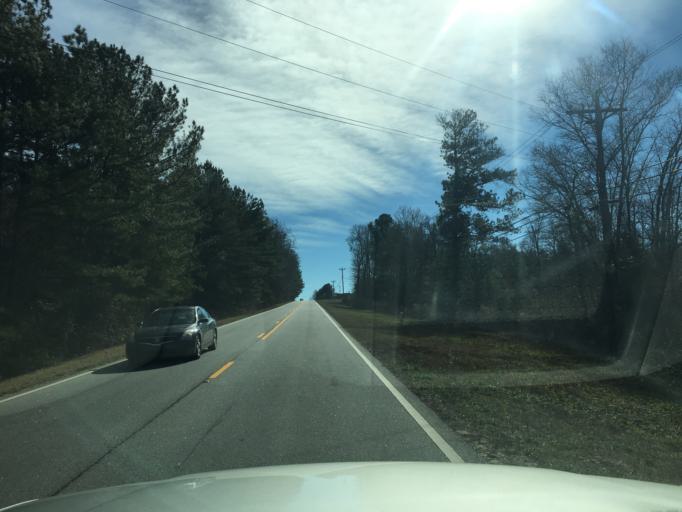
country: US
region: Georgia
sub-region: Rockdale County
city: Lakeview Estates
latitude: 33.6966
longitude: -84.0222
